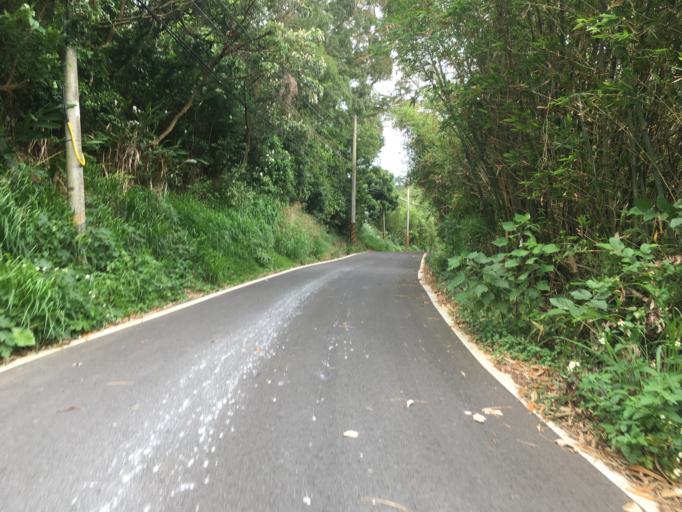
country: TW
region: Taiwan
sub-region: Hsinchu
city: Hsinchu
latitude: 24.7463
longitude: 120.9844
